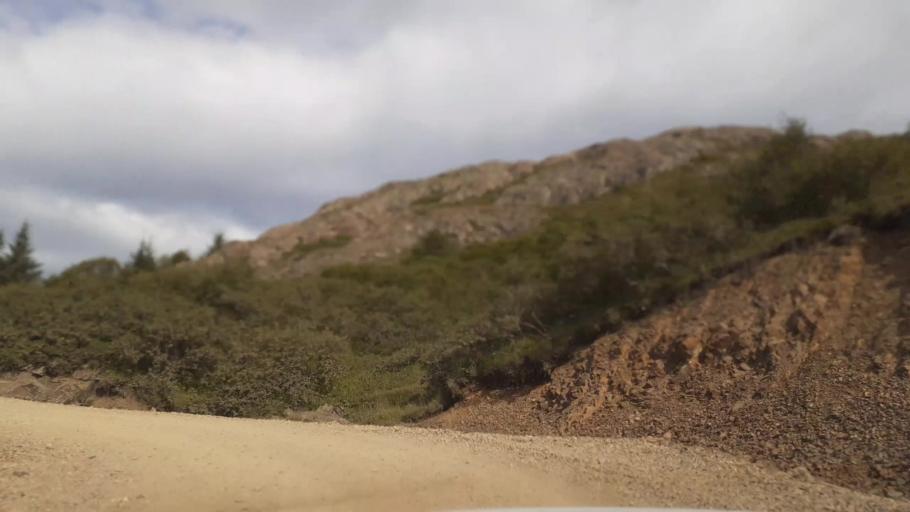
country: IS
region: East
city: Hoefn
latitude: 64.4384
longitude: -14.9125
